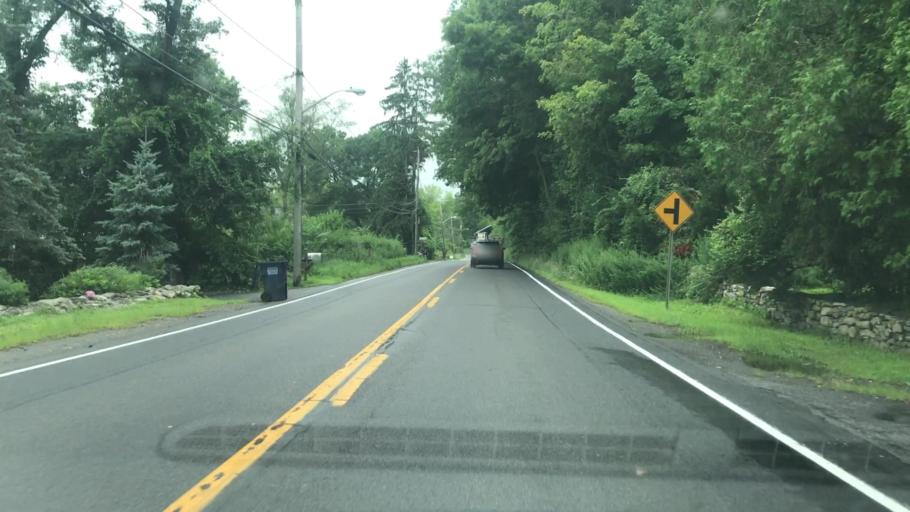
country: US
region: New York
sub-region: Westchester County
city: Jefferson Valley-Yorktown
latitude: 41.3442
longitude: -73.7860
